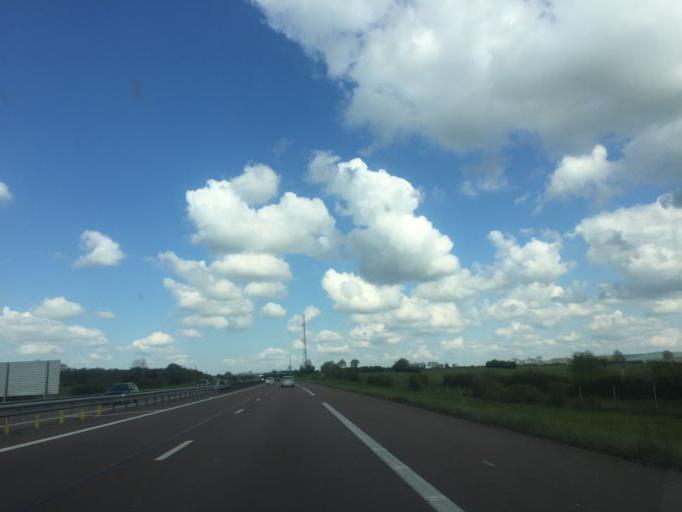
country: FR
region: Bourgogne
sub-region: Departement de la Cote-d'Or
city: Vitteaux
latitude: 47.3436
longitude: 4.4635
